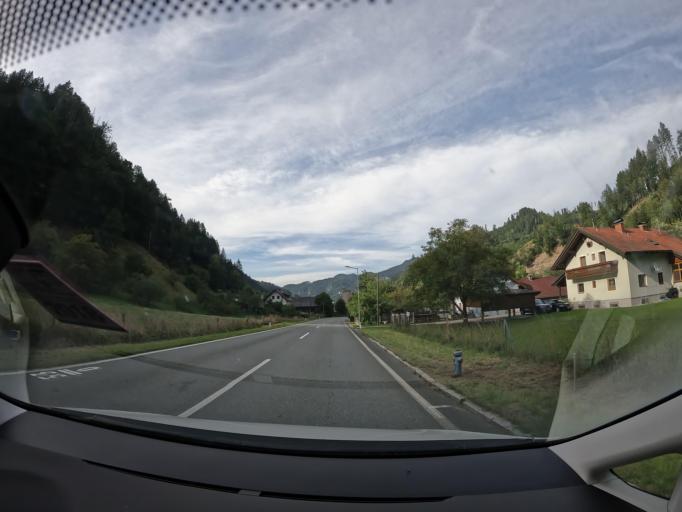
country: AT
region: Carinthia
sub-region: Politischer Bezirk Volkermarkt
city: Bad Eisenkappel
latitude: 46.4689
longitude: 14.5925
